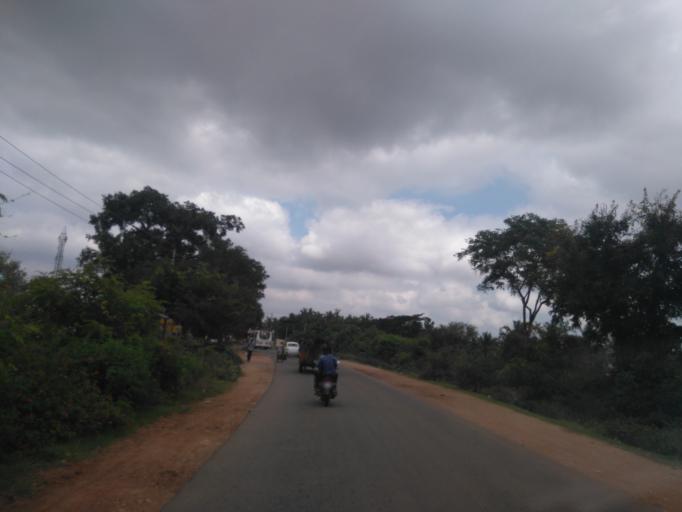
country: IN
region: Karnataka
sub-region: Mysore
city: Mysore
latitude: 12.2889
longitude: 76.7146
